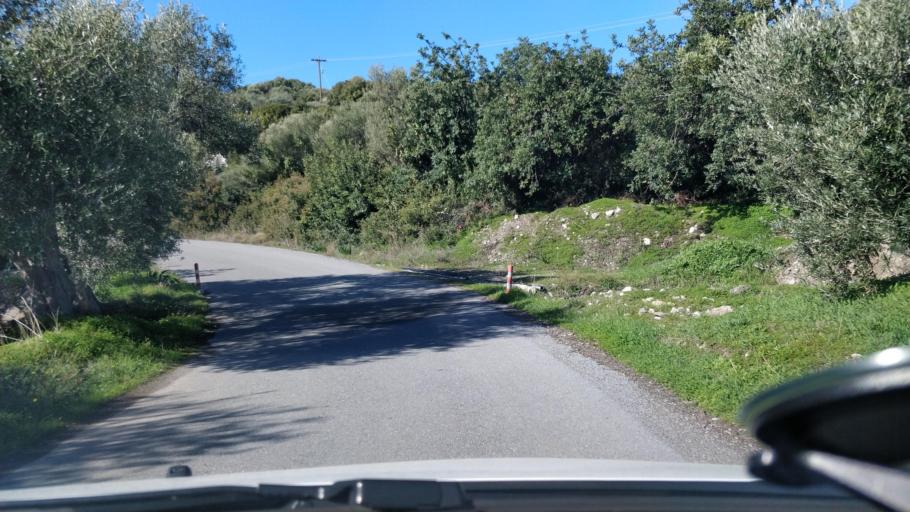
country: GR
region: Crete
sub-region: Nomos Lasithiou
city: Gra Liyia
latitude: 35.0200
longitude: 25.5545
